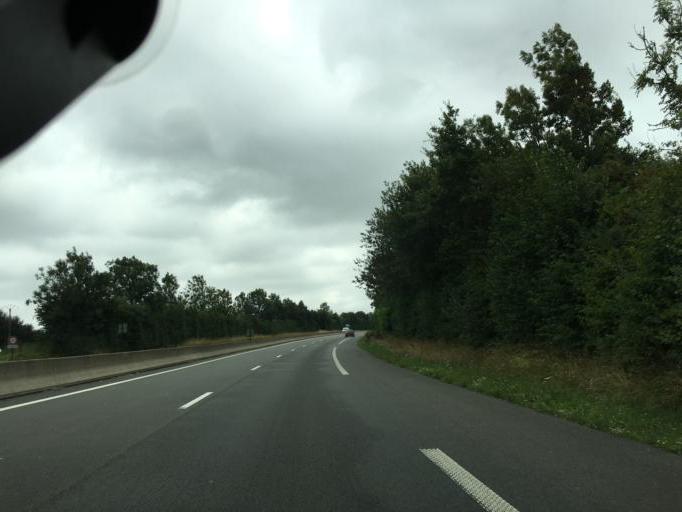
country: FR
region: Nord-Pas-de-Calais
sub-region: Departement du Pas-de-Calais
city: Saint-Pol-sur-Ternoise
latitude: 50.3766
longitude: 2.2969
